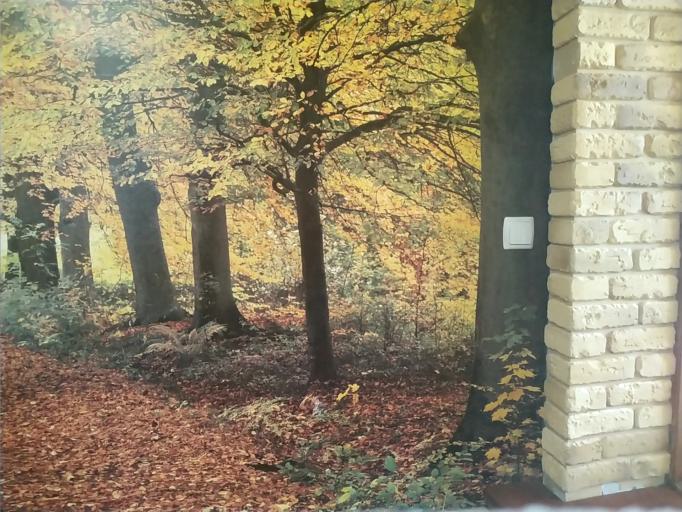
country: RU
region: Tverskaya
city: Vyshniy Volochek
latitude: 57.6127
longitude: 34.5945
